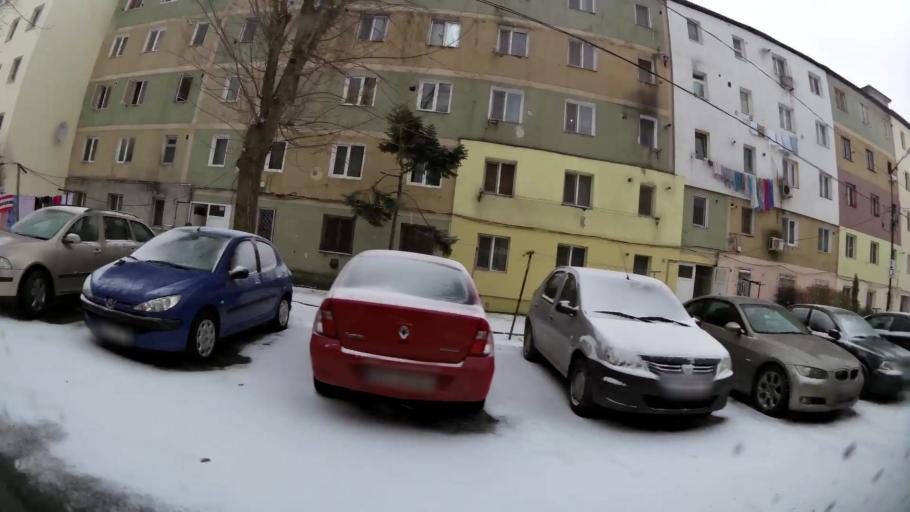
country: RO
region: Dambovita
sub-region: Municipiul Targoviste
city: Targoviste
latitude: 44.9227
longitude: 25.4691
